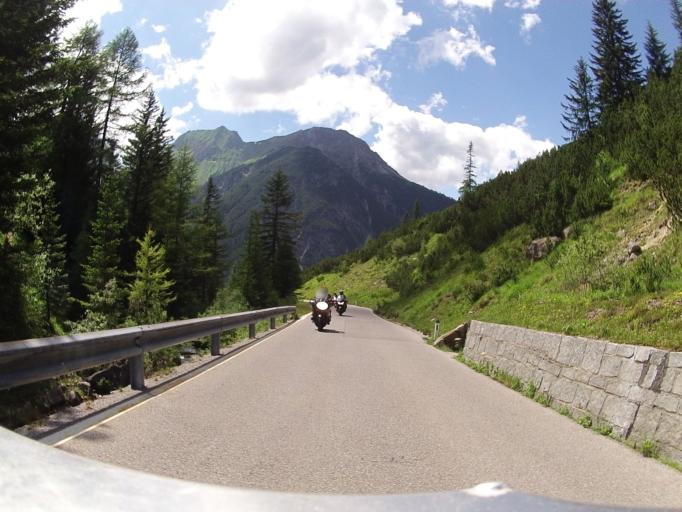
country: AT
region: Tyrol
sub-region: Politischer Bezirk Reutte
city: Namlos
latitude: 47.2834
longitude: 10.6189
